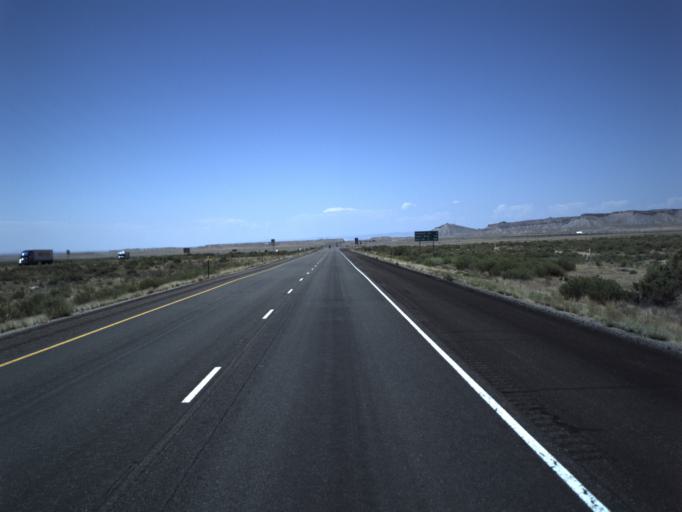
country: US
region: Utah
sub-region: Grand County
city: Moab
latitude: 38.9582
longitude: -109.7413
